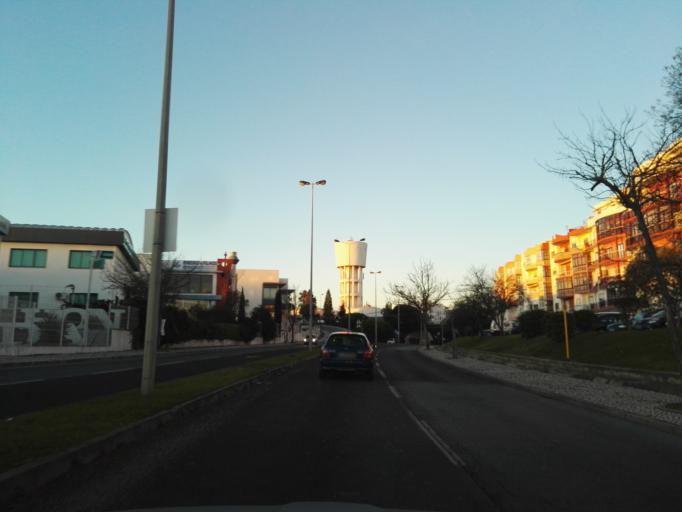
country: PT
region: Setubal
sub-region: Seixal
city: Corroios
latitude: 38.6534
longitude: -9.1668
